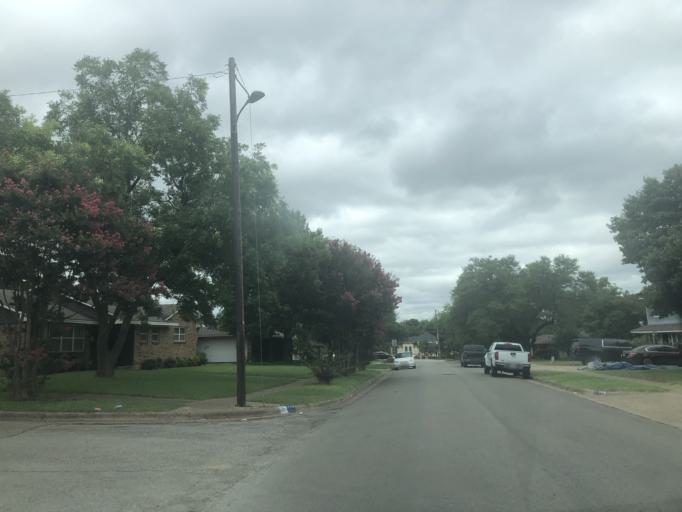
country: US
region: Texas
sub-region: Dallas County
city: Duncanville
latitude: 32.6528
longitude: -96.9169
